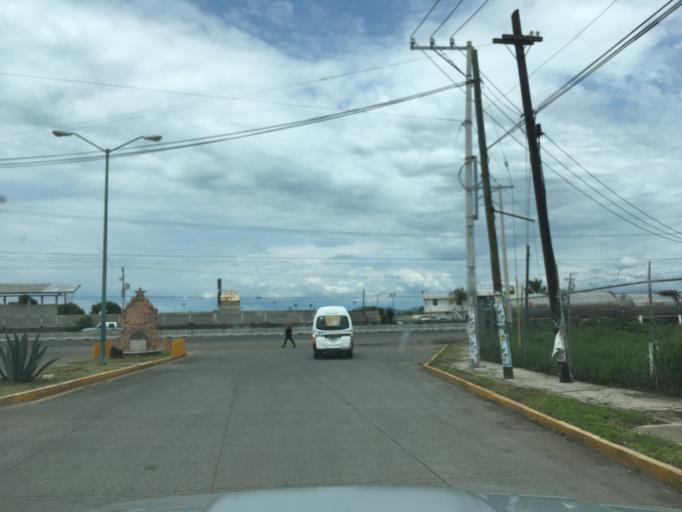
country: MX
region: Michoacan
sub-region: Tarimbaro
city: Meson Nuevo (Canada de la Magdalena)
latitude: 19.7972
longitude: -101.1631
